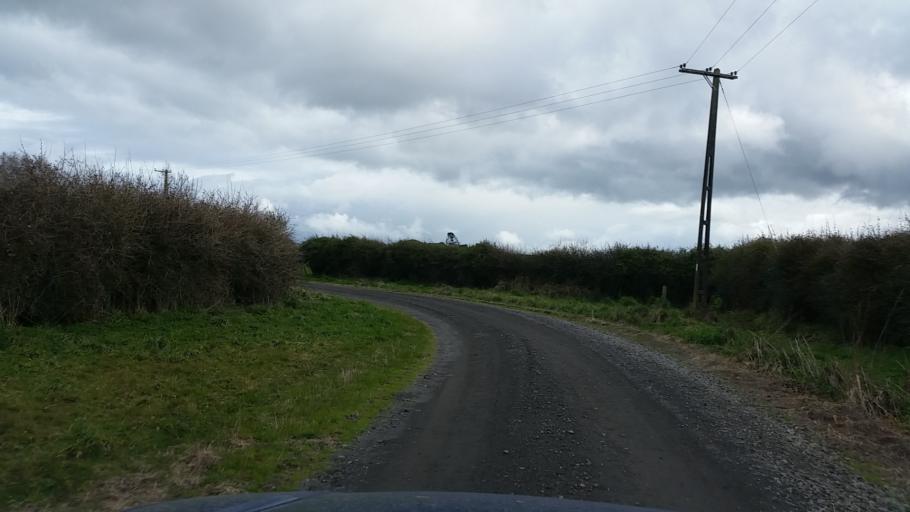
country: NZ
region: Taranaki
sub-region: South Taranaki District
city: Eltham
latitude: -39.3567
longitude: 174.3814
